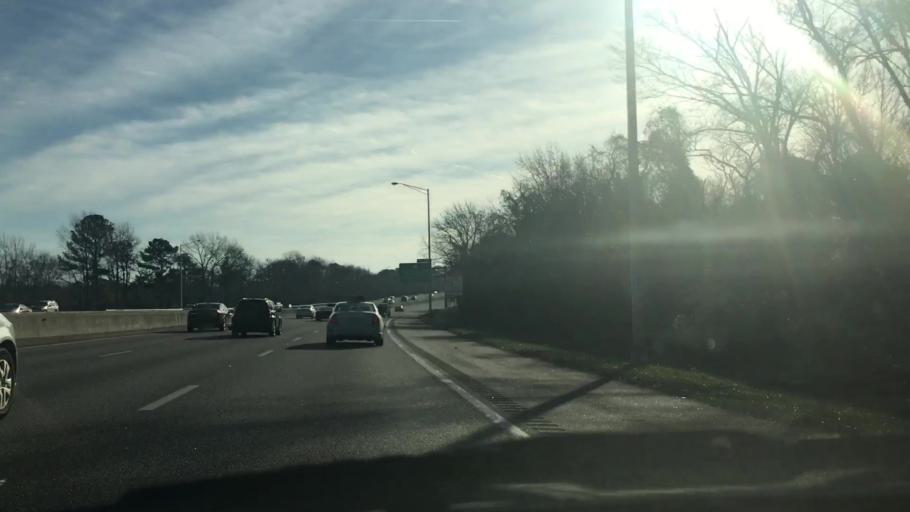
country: US
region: Virginia
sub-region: City of Norfolk
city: Norfolk
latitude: 36.8791
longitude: -76.2033
